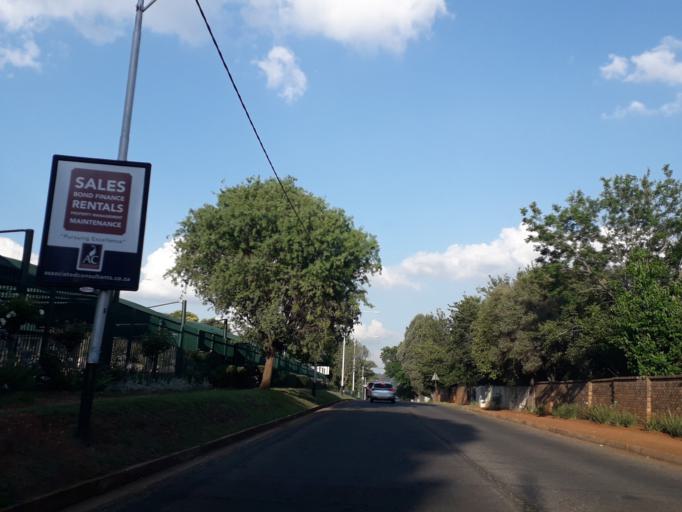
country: ZA
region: Gauteng
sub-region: City of Johannesburg Metropolitan Municipality
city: Johannesburg
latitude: -26.1378
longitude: 28.0032
